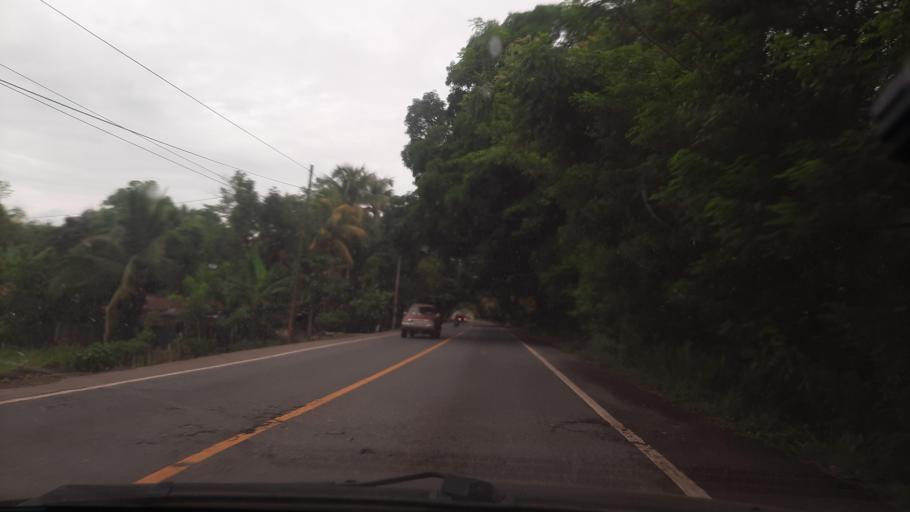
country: GT
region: Izabal
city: Morales
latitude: 15.4447
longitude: -88.9470
